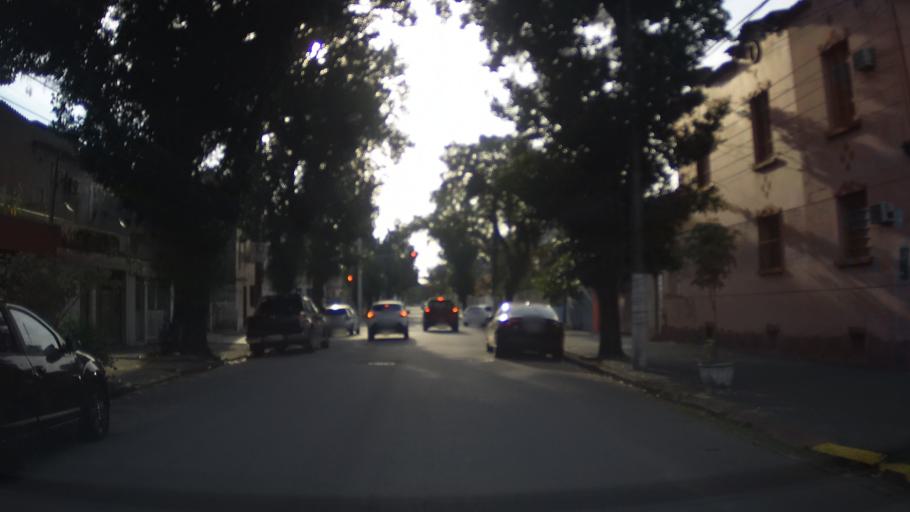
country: BR
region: Sao Paulo
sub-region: Santos
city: Santos
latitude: -23.9490
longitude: -46.3243
